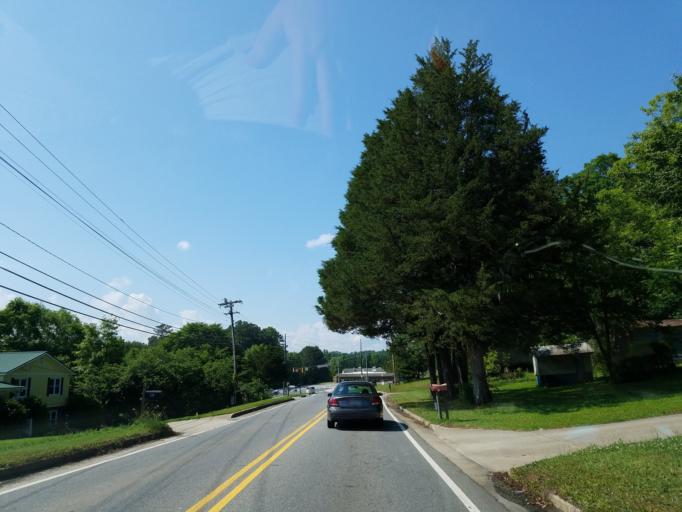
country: US
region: Georgia
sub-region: Cherokee County
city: Woodstock
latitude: 34.1289
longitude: -84.4937
